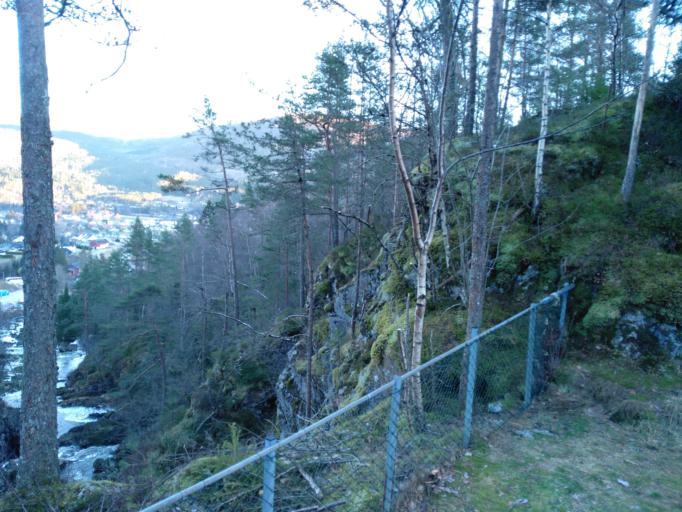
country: NO
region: Vest-Agder
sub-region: Sirdal
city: Tonstad
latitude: 58.6667
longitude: 6.6954
